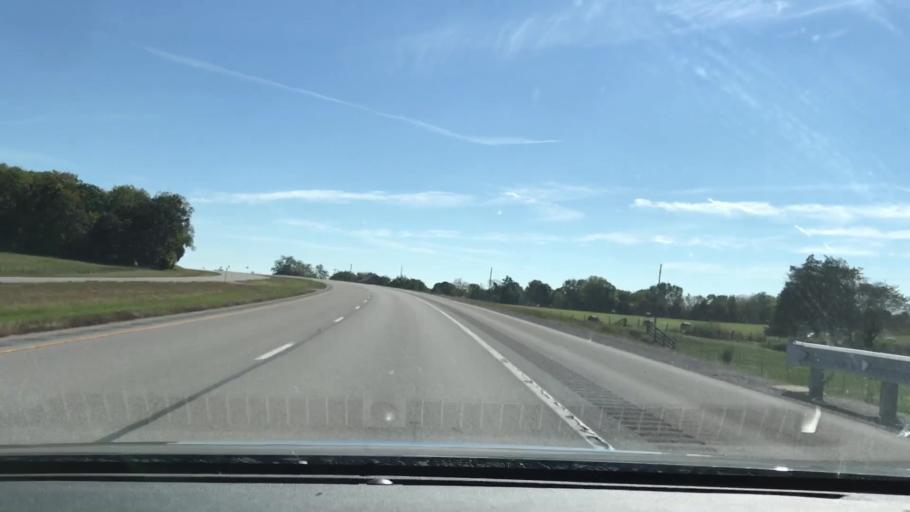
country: US
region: Kentucky
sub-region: Todd County
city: Elkton
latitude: 36.8099
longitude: -87.1350
